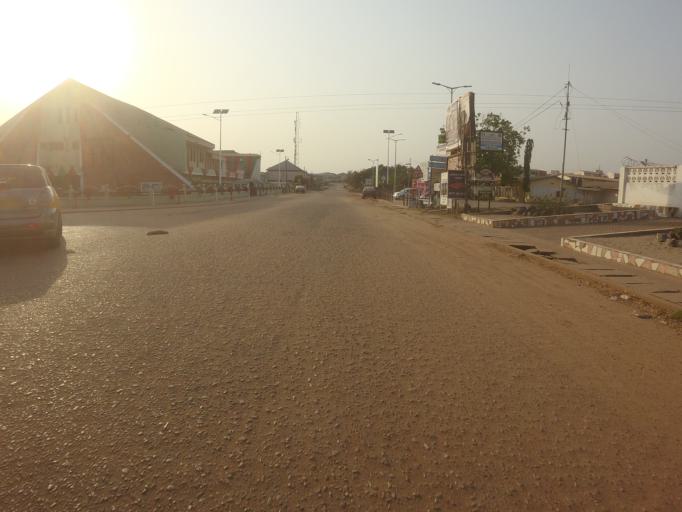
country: GH
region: Greater Accra
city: Nungua
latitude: 5.6233
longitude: -0.0609
